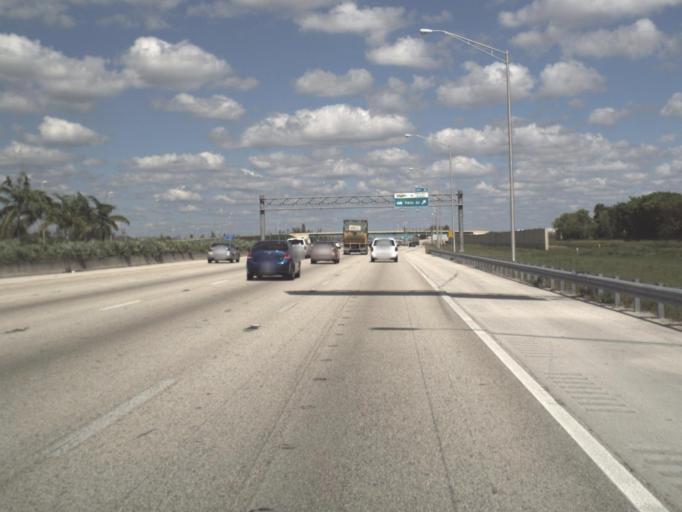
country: US
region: Florida
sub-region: Miami-Dade County
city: Doral
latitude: 25.8333
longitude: -80.3867
